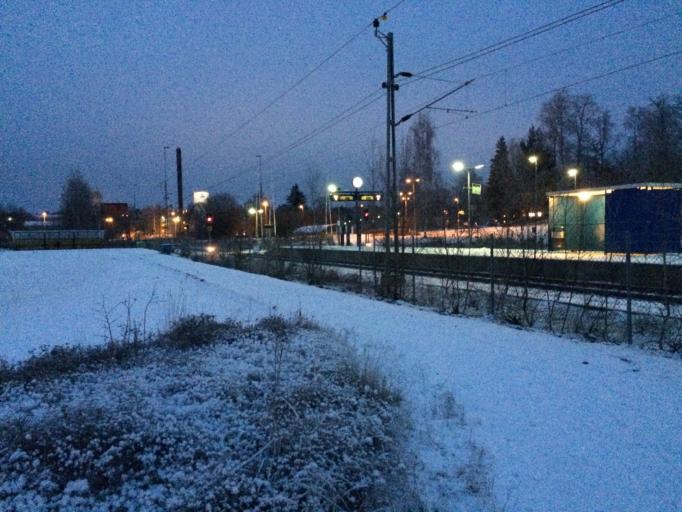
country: SE
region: Vaestmanland
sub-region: Hallstahammars Kommun
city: Hallstahammar
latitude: 59.6146
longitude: 16.2199
